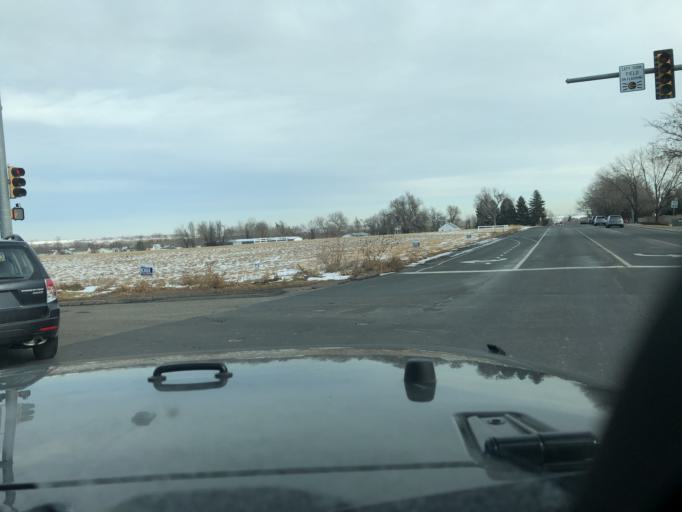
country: US
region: Colorado
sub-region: Boulder County
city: Longmont
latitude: 40.1740
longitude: -105.0743
